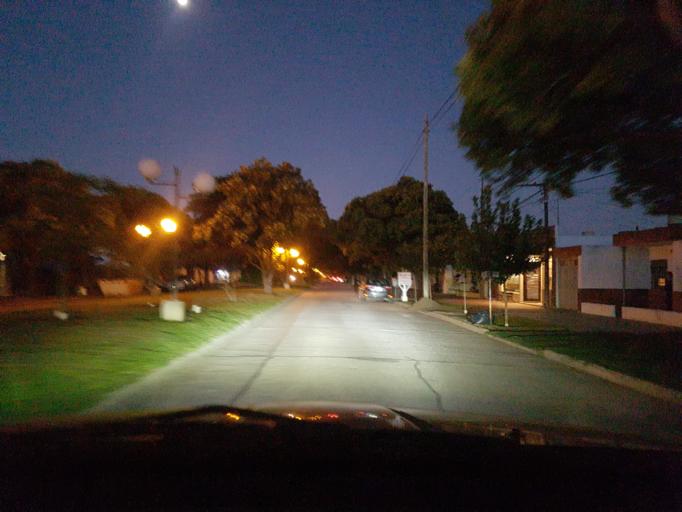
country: AR
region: Cordoba
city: General Cabrera
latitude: -32.7605
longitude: -63.7877
